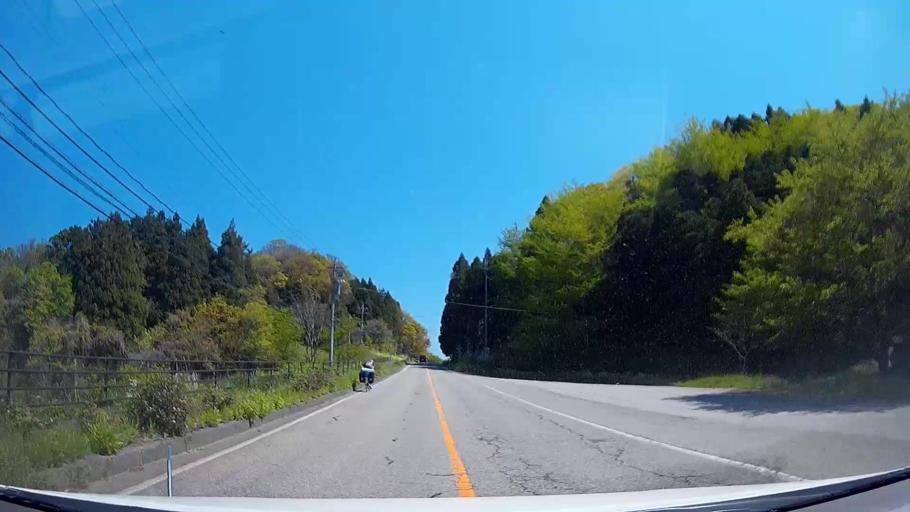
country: JP
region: Ishikawa
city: Nanao
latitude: 37.4109
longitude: 136.9744
